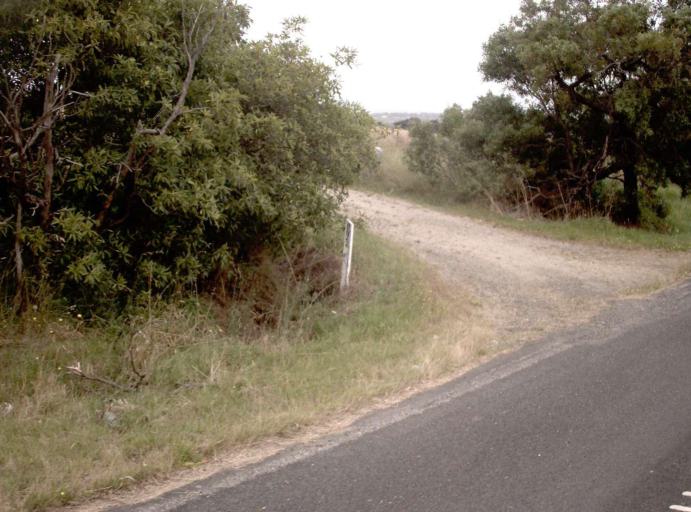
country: AU
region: Victoria
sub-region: Cardinia
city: Pakenham Upper
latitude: -38.0663
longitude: 145.5496
